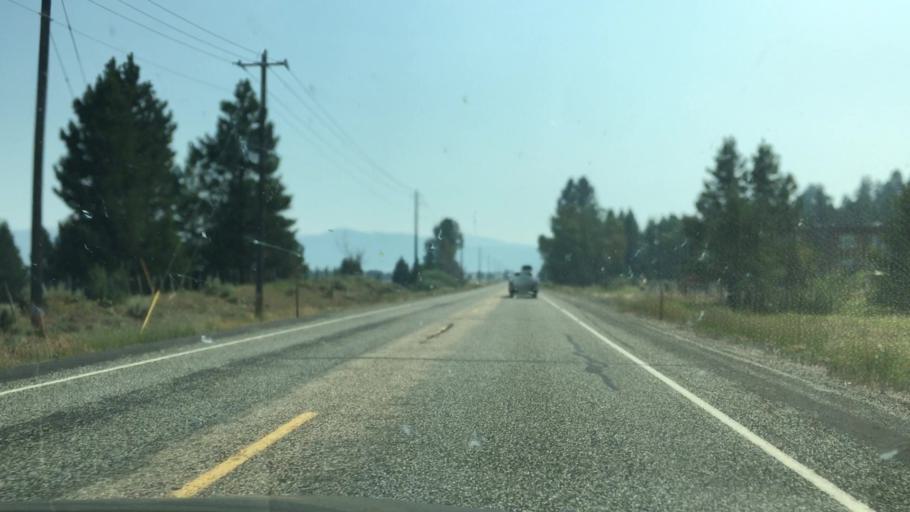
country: US
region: Idaho
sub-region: Valley County
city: Cascade
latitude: 44.3646
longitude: -116.0193
